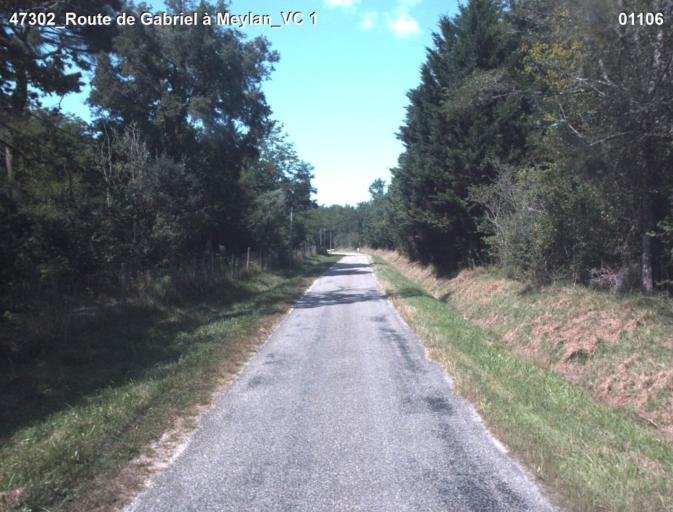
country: FR
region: Aquitaine
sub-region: Departement du Lot-et-Garonne
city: Mezin
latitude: 44.0616
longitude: 0.1434
